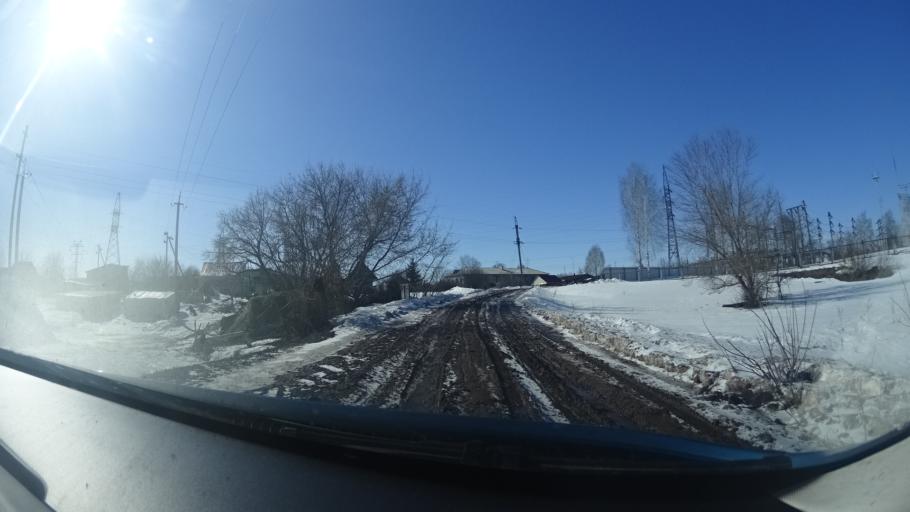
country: RU
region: Bashkortostan
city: Chishmy
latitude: 54.5840
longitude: 55.3979
